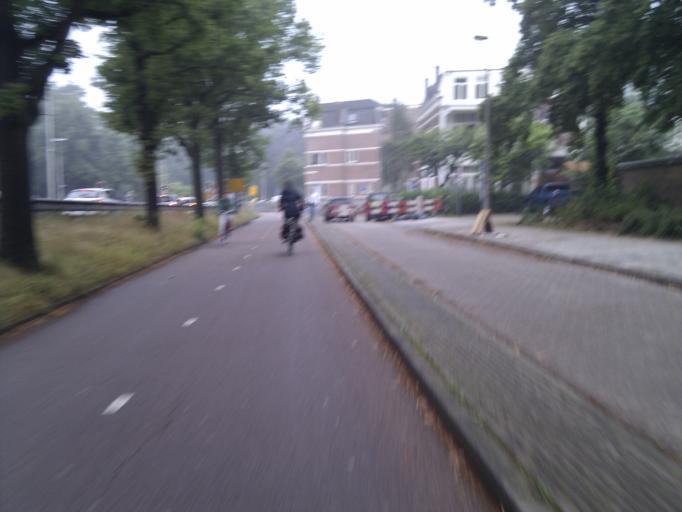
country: NL
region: Utrecht
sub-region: Gemeente Utrecht
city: Utrecht
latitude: 52.0961
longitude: 5.1423
